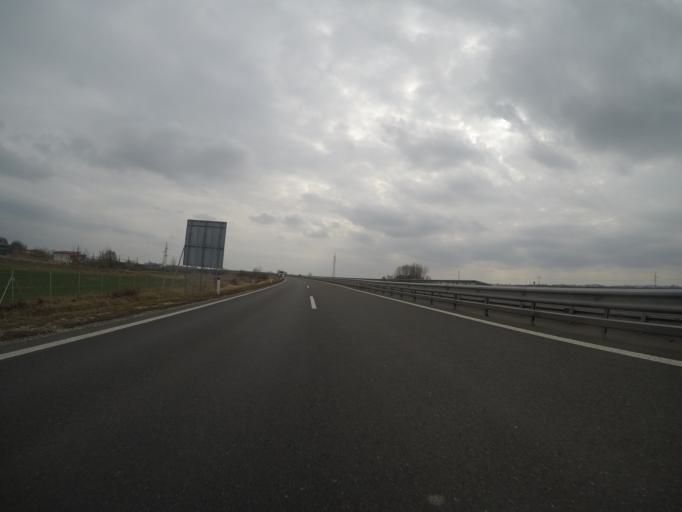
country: SI
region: Lendava-Lendva
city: Lendava
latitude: 46.5410
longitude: 16.4407
